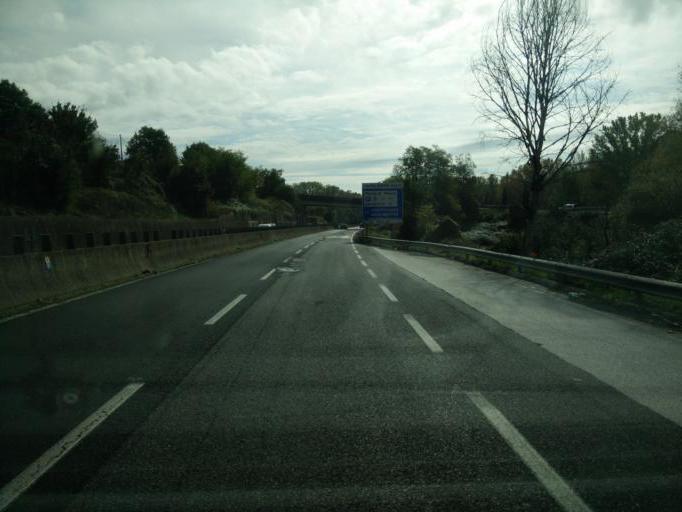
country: IT
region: Tuscany
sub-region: Provincia di Siena
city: Siena
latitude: 43.3123
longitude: 11.3104
